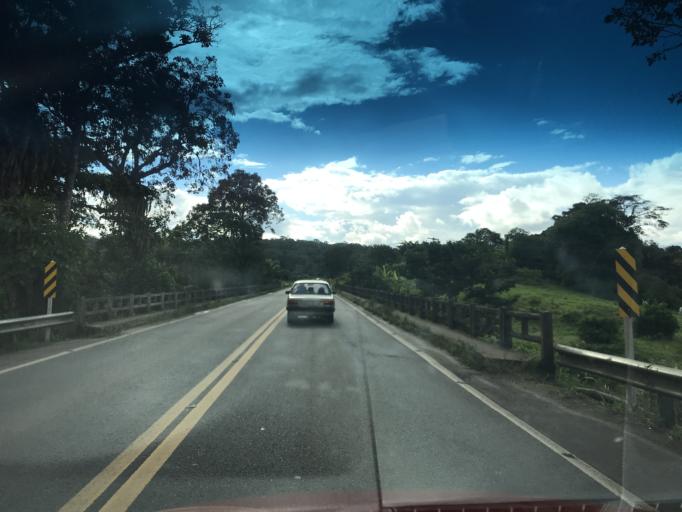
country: BR
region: Bahia
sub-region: Ibirapitanga
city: Ibirapitanga
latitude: -14.1505
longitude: -39.3461
